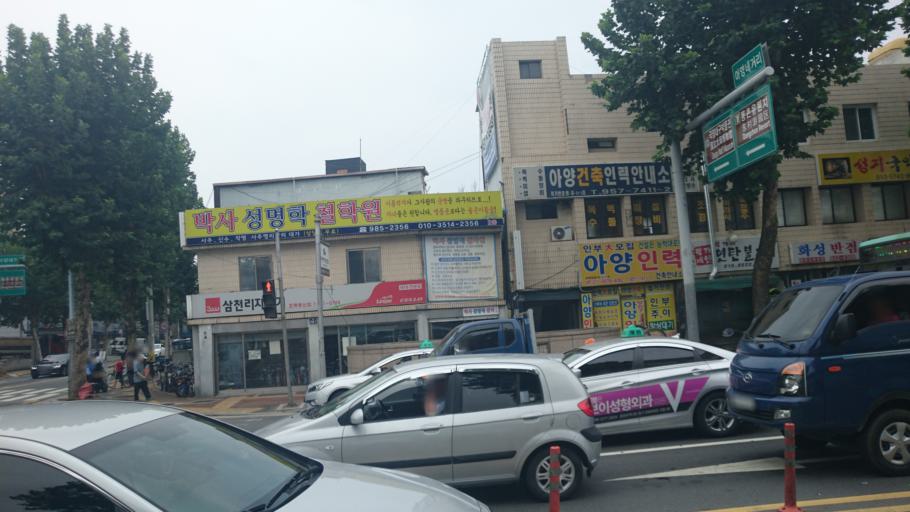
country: KR
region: Daegu
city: Daegu
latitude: 35.8875
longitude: 128.6406
